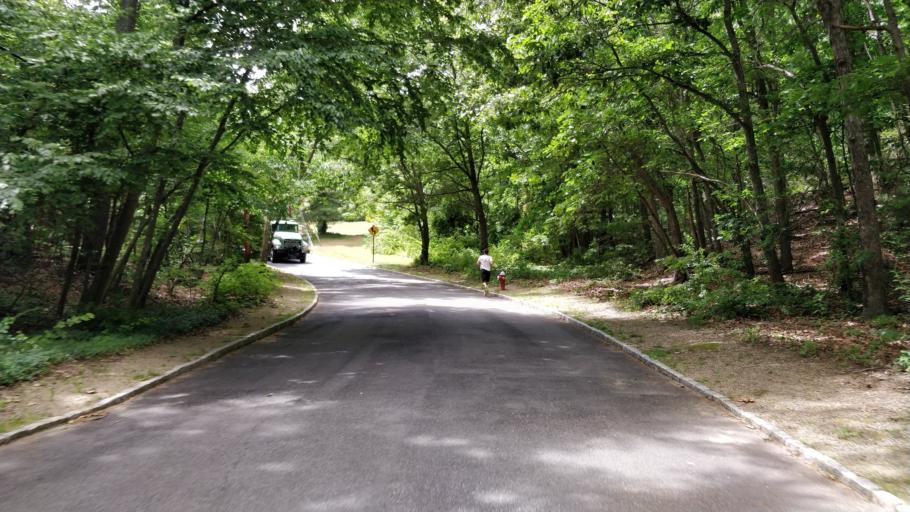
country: US
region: New York
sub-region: Nassau County
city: Laurel Hollow
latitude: 40.8436
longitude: -73.4697
